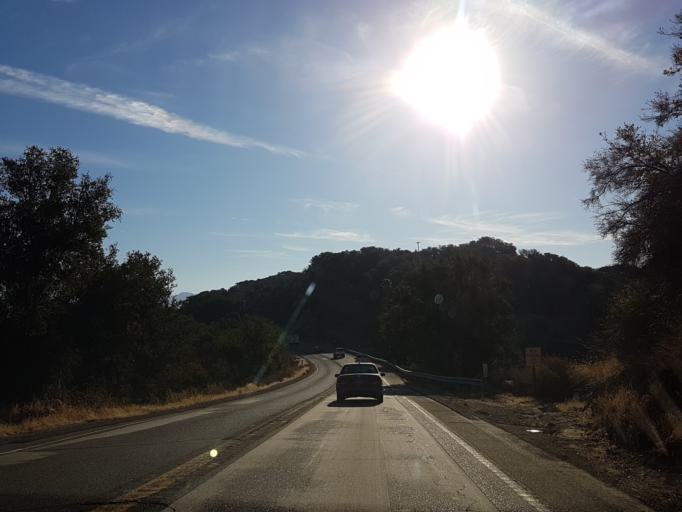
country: US
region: California
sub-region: Santa Barbara County
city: Goleta
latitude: 34.5618
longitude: -119.9269
